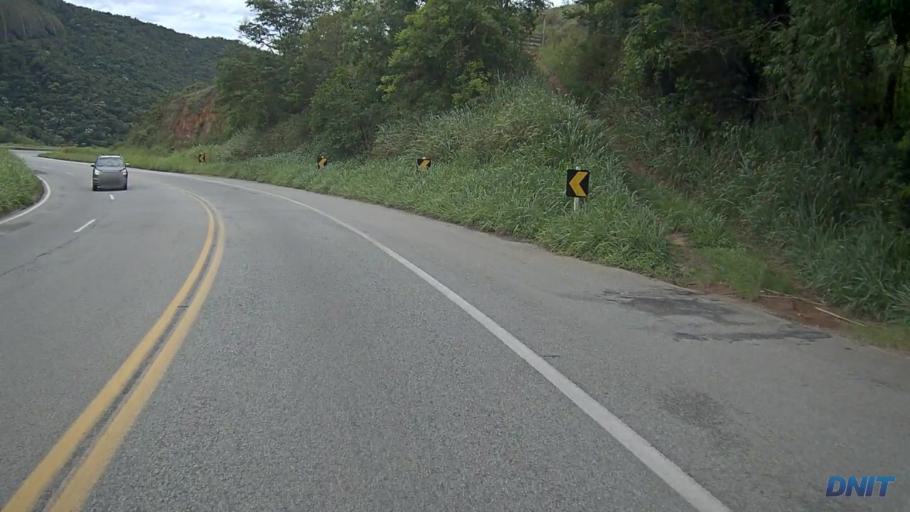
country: BR
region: Minas Gerais
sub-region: Nova Era
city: Nova Era
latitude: -19.6497
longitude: -42.9404
